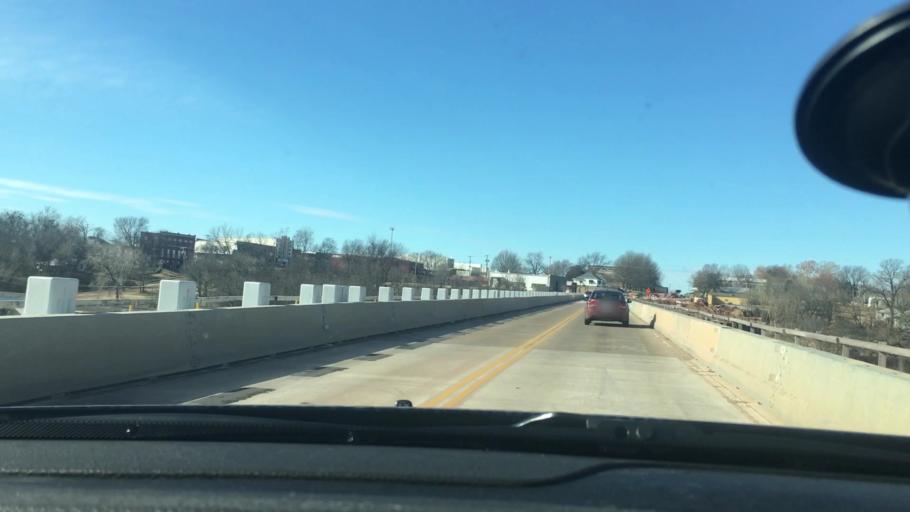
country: US
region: Oklahoma
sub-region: McClain County
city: Purcell
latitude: 35.0138
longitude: -97.3557
